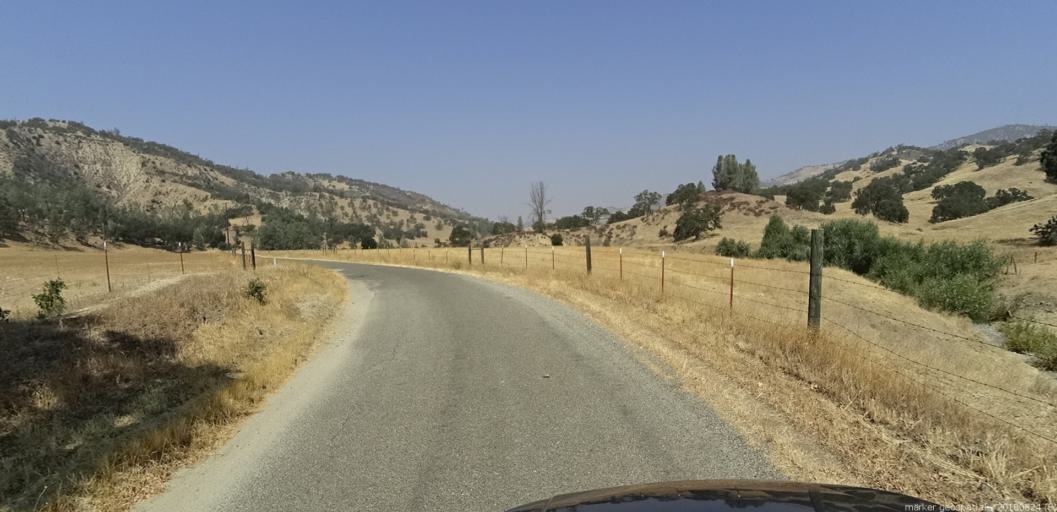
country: US
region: California
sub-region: Fresno County
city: Coalinga
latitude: 36.0756
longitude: -120.6556
